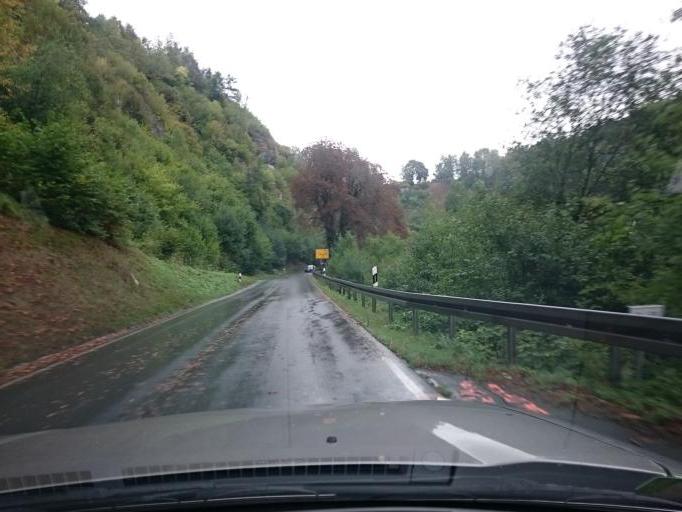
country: DE
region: Bavaria
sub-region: Upper Franconia
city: Pottenstein
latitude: 49.7664
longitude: 11.4090
